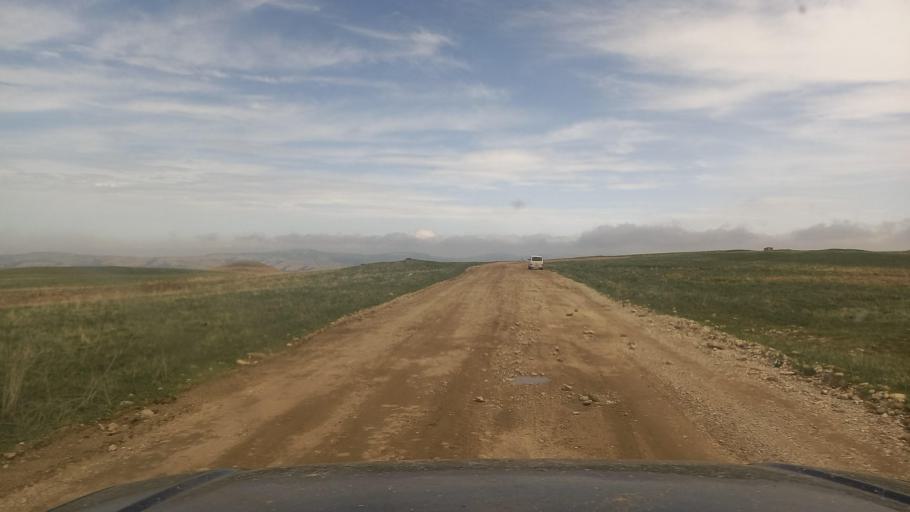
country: RU
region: Stavropol'skiy
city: Kislovodsk
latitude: 43.7646
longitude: 42.8144
